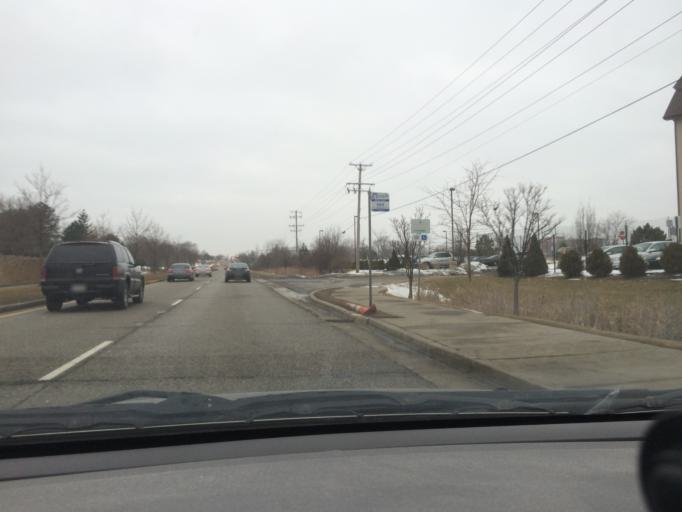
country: US
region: Illinois
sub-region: Cook County
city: South Barrington
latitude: 42.0471
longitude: -88.1332
